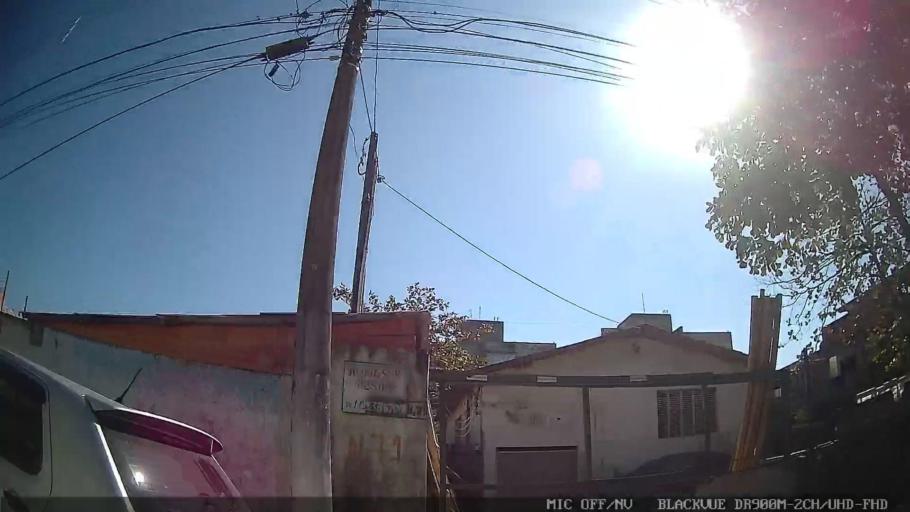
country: BR
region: Sao Paulo
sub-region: Guaruja
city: Guaruja
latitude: -23.9856
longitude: -46.2022
